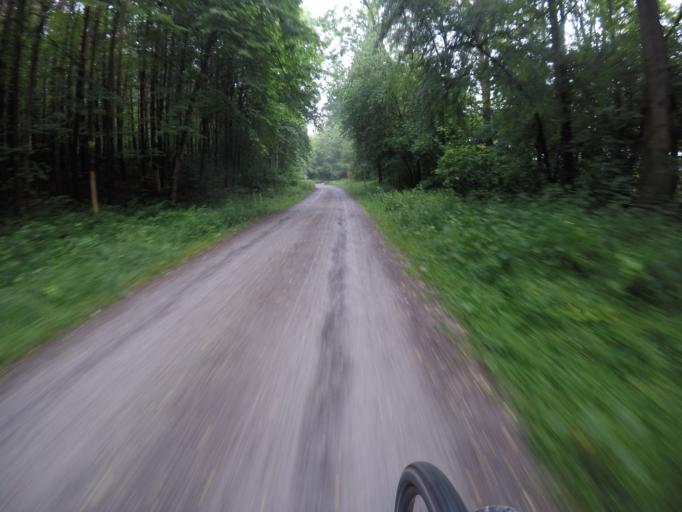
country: DE
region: Baden-Wuerttemberg
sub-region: Regierungsbezirk Stuttgart
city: Sindelfingen
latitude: 48.7243
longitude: 9.0797
